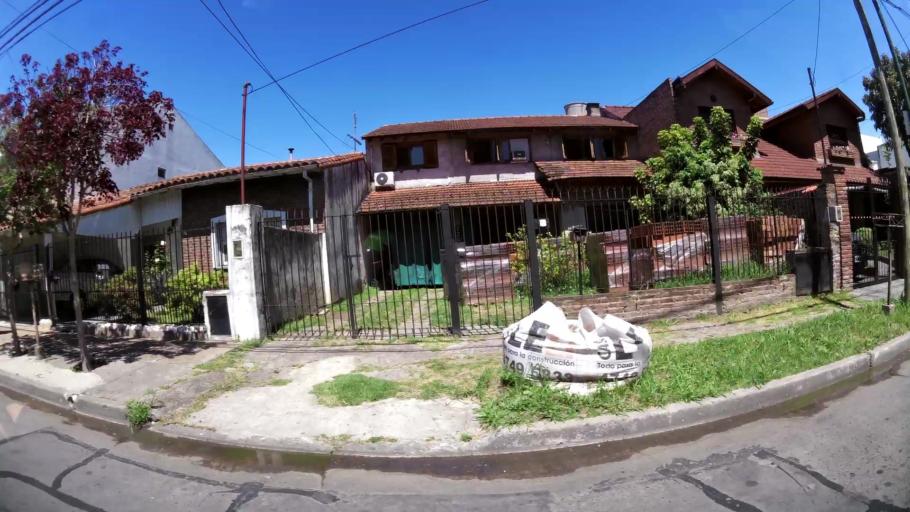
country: AR
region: Buenos Aires
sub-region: Partido de General San Martin
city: General San Martin
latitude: -34.5242
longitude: -58.5507
